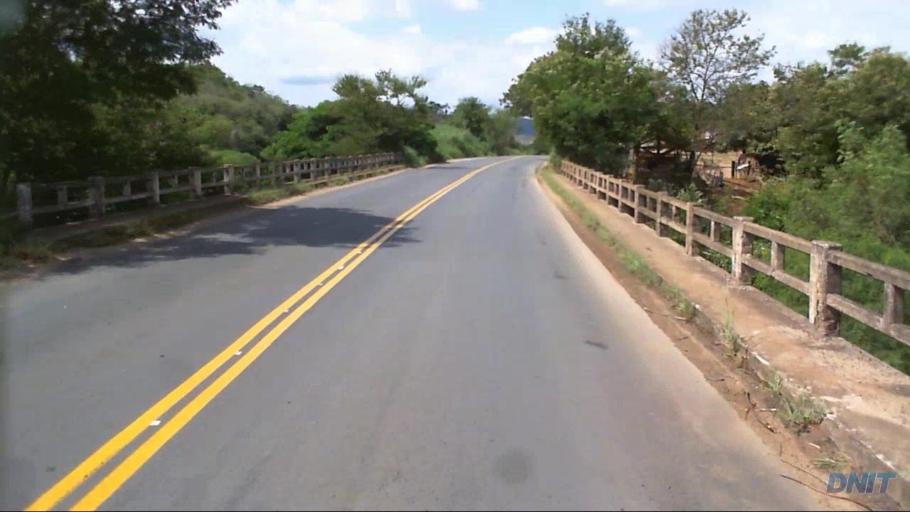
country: BR
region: Minas Gerais
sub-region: Governador Valadares
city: Governador Valadares
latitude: -18.9134
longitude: -42.0045
